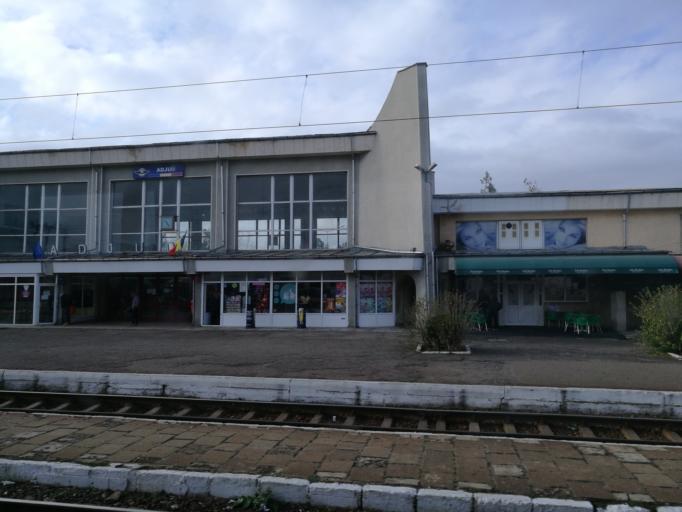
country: RO
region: Vrancea
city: Adjud
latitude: 46.0984
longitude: 27.1926
